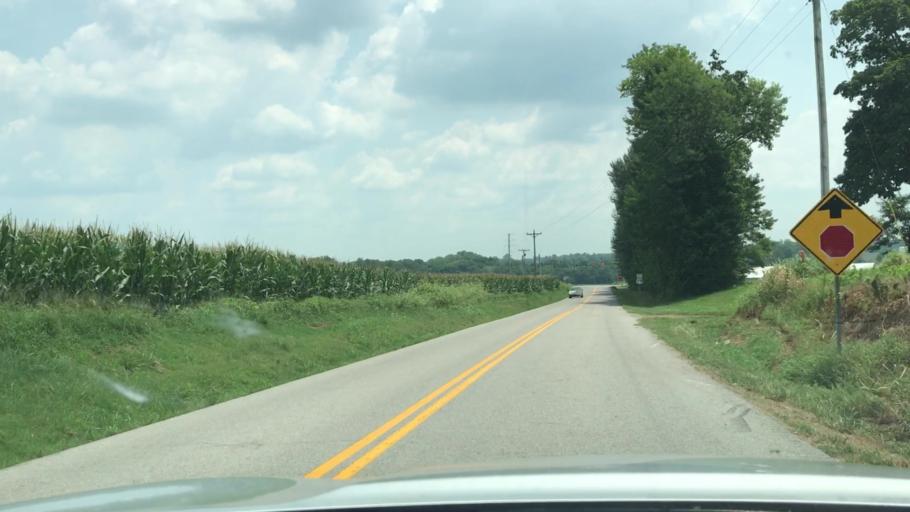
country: US
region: Kentucky
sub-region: Todd County
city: Elkton
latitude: 36.7263
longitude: -87.0887
